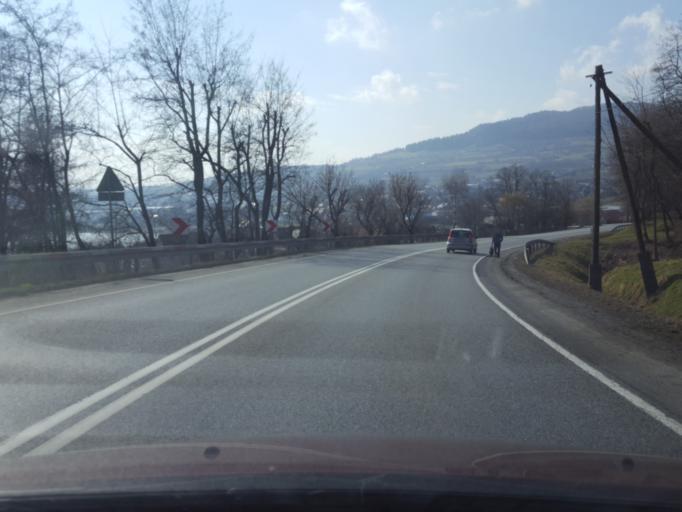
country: PL
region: Lesser Poland Voivodeship
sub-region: Powiat nowosadecki
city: Lososina Dolna
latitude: 49.7181
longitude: 20.6417
